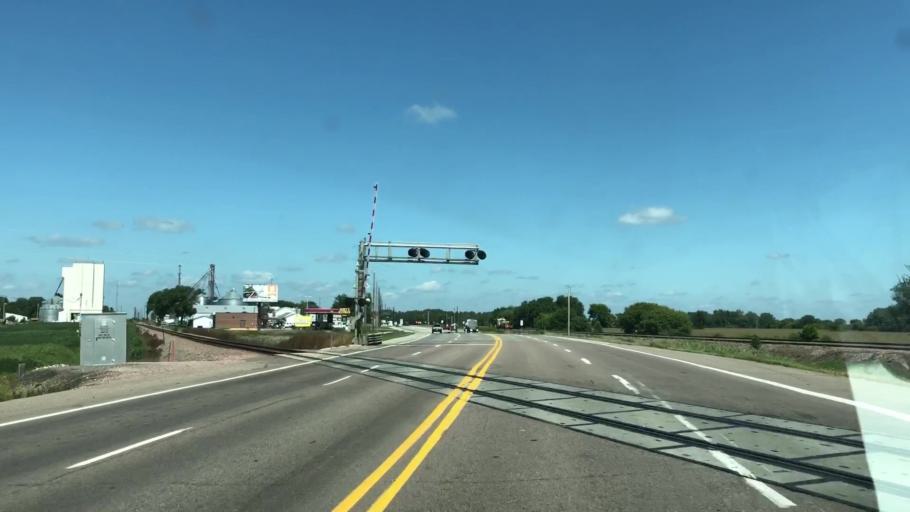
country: US
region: Iowa
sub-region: Plymouth County
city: Le Mars
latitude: 42.7150
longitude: -96.2492
